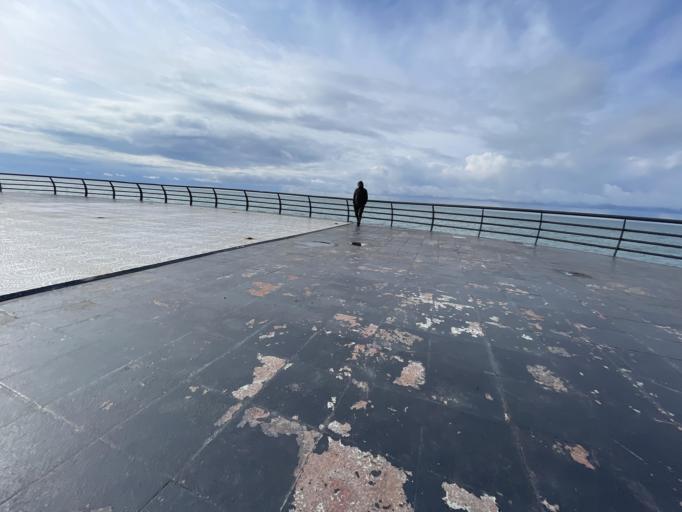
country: GE
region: Ajaria
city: Batumi
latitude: 41.6565
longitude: 41.6333
